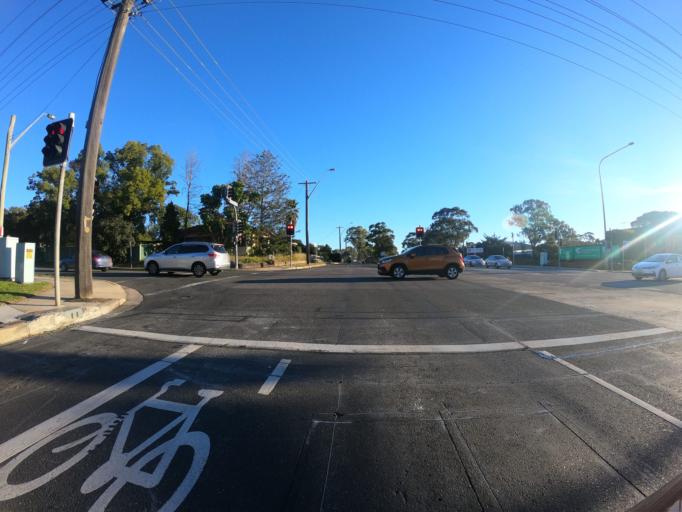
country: AU
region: New South Wales
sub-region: Campbelltown Municipality
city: Campbelltown
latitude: -34.0666
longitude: 150.8197
